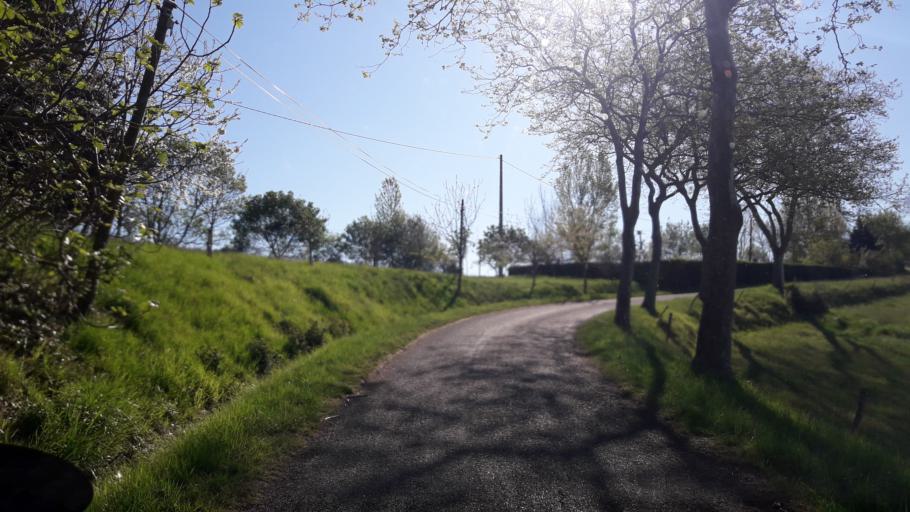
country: FR
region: Midi-Pyrenees
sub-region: Departement de la Haute-Garonne
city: Montesquieu-Volvestre
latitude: 43.2020
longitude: 1.2772
